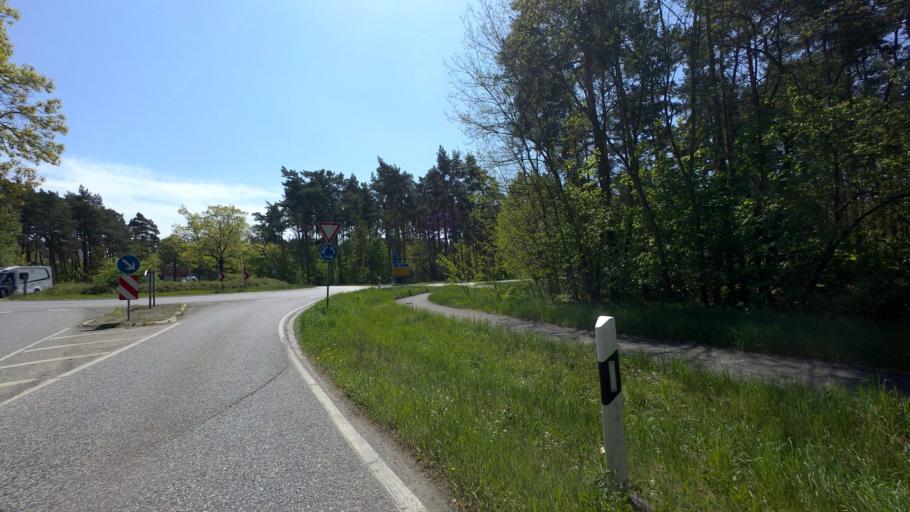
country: DE
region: Brandenburg
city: Bestensee
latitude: 52.2422
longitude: 13.6629
